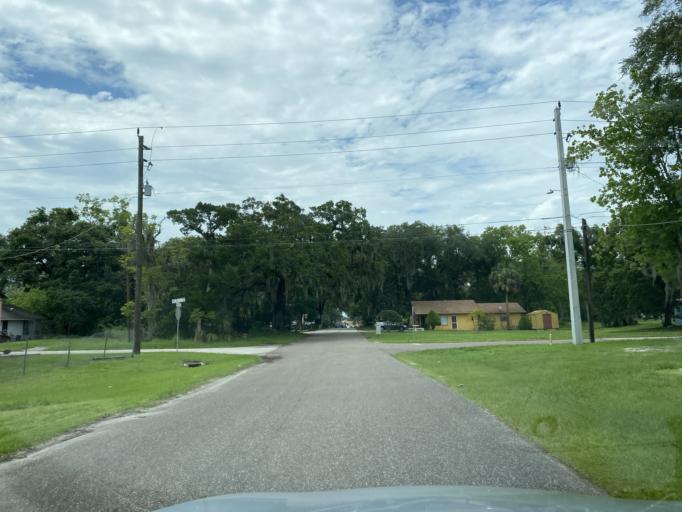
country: US
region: Florida
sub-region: Seminole County
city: Sanford
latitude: 28.8078
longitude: -81.2628
